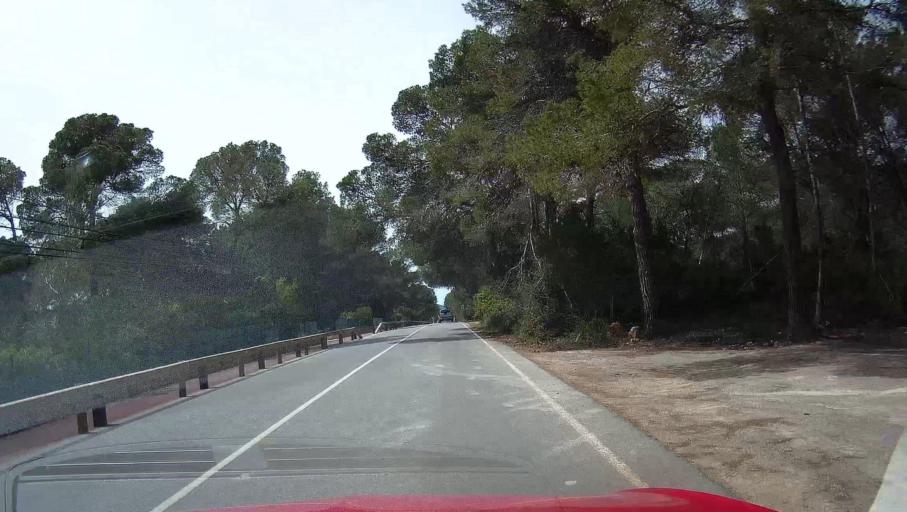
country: ES
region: Balearic Islands
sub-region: Illes Balears
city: Santa Eularia des Riu
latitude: 39.0005
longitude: 1.5631
